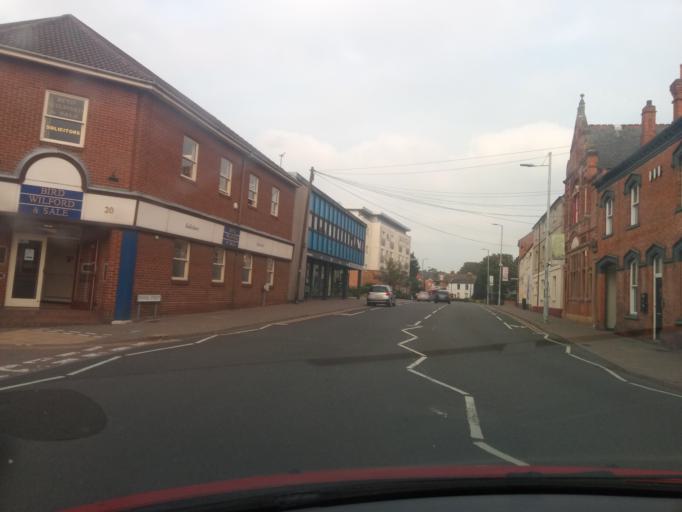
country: GB
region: England
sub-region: Leicestershire
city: Loughborough
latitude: 52.7737
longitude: -1.2055
